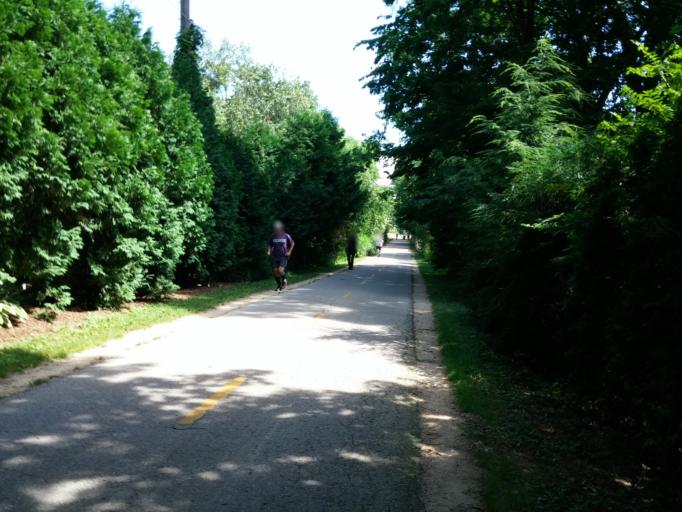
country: US
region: Wisconsin
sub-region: Dane County
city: Shorewood Hills
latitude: 43.0617
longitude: -89.4276
